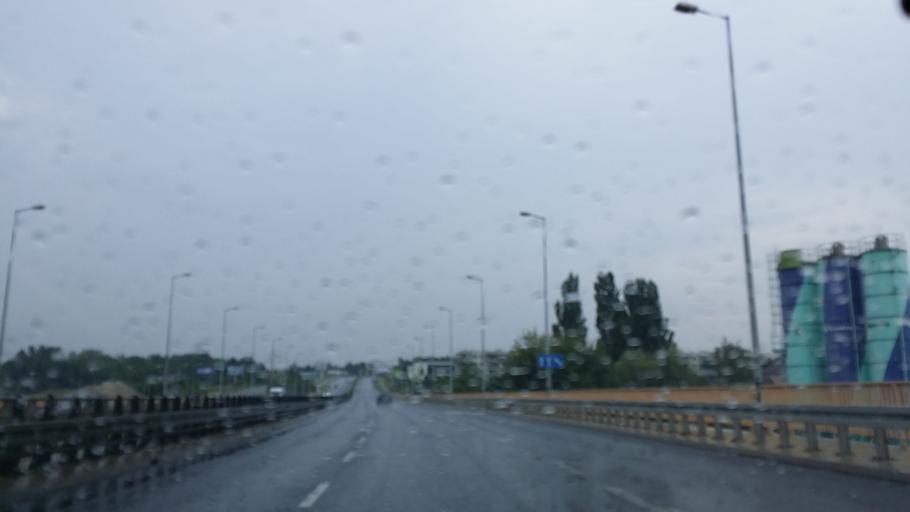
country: PL
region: Lesser Poland Voivodeship
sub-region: Krakow
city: Krakow
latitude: 50.0281
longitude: 19.9445
